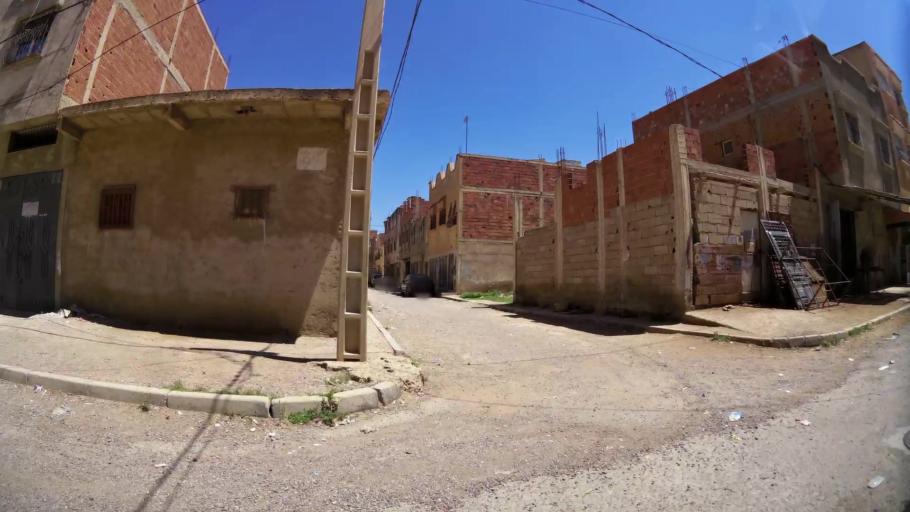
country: MA
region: Oriental
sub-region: Oujda-Angad
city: Oujda
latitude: 34.6566
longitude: -1.9266
